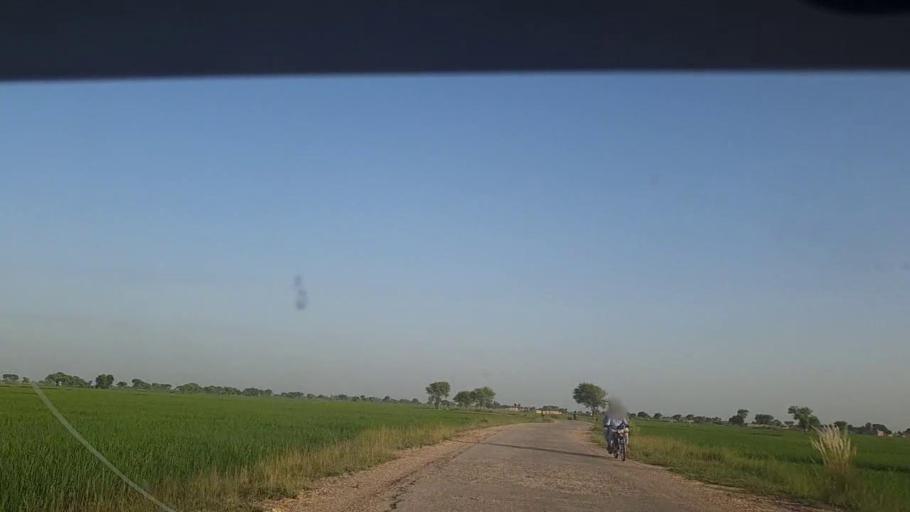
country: PK
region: Sindh
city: Thul
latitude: 28.1368
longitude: 68.8873
